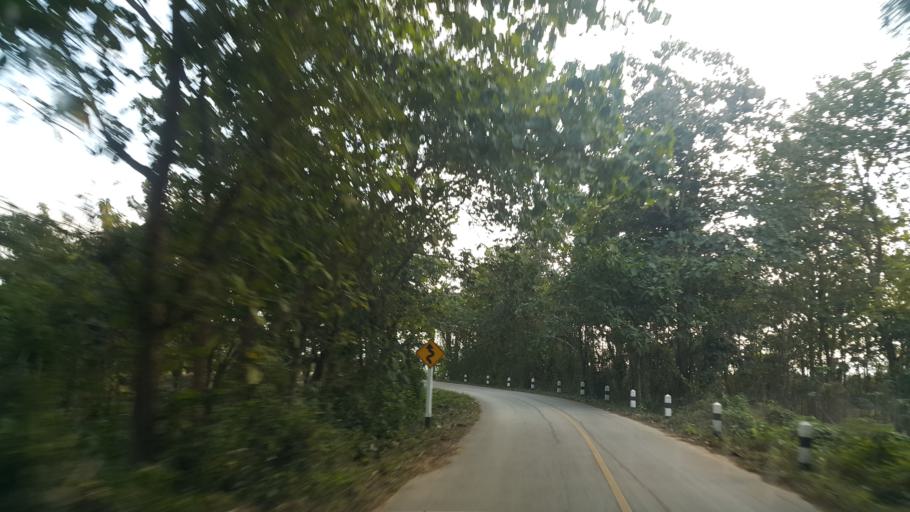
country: TH
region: Lampang
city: Sop Prap
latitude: 17.9203
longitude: 99.3280
